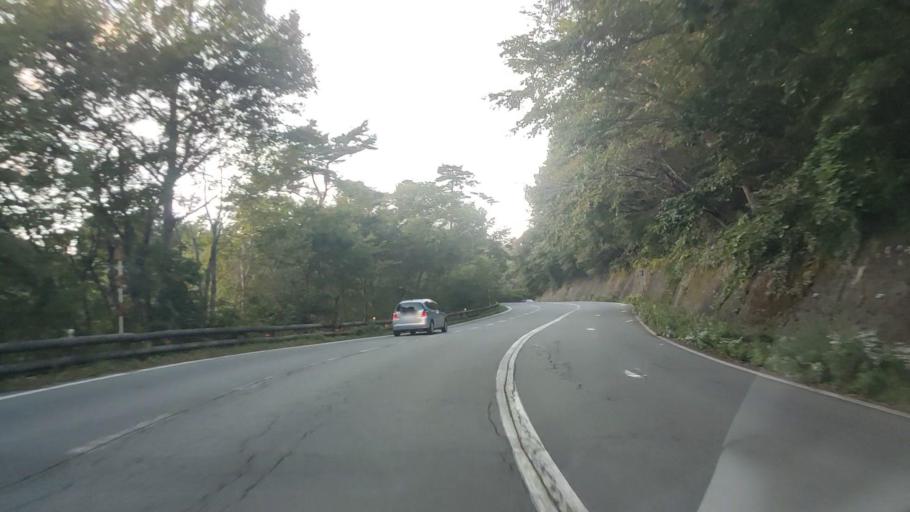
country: JP
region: Nagano
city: Komoro
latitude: 36.3831
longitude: 138.5884
